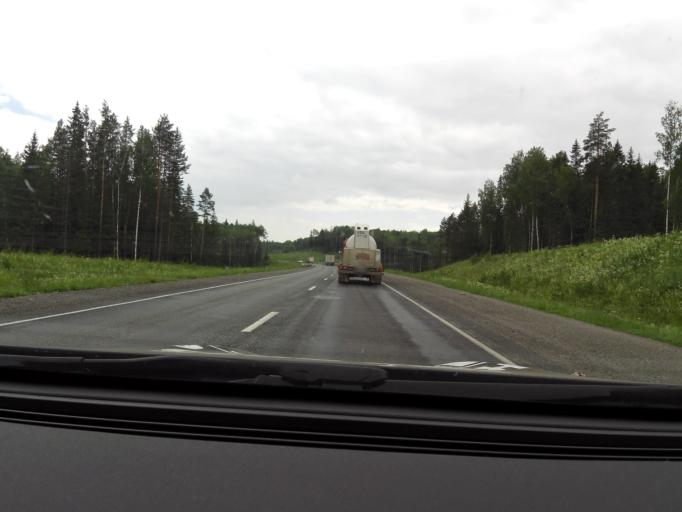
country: RU
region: Perm
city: Suksun
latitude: 57.1088
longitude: 57.3075
